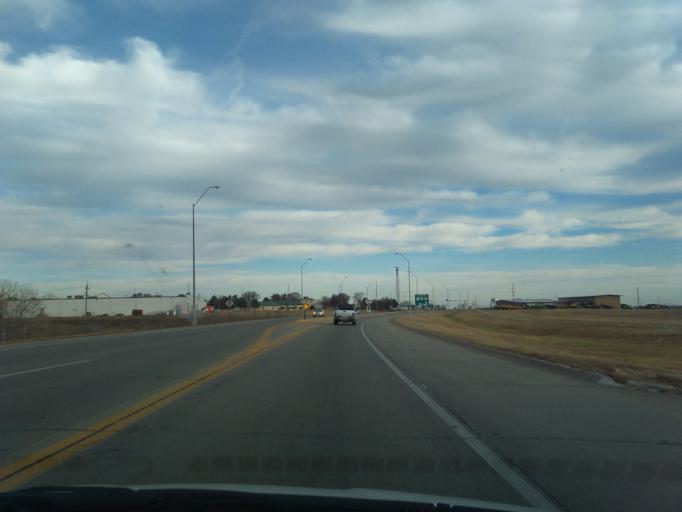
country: US
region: Nebraska
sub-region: Red Willow County
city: McCook
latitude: 40.2003
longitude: -100.6496
